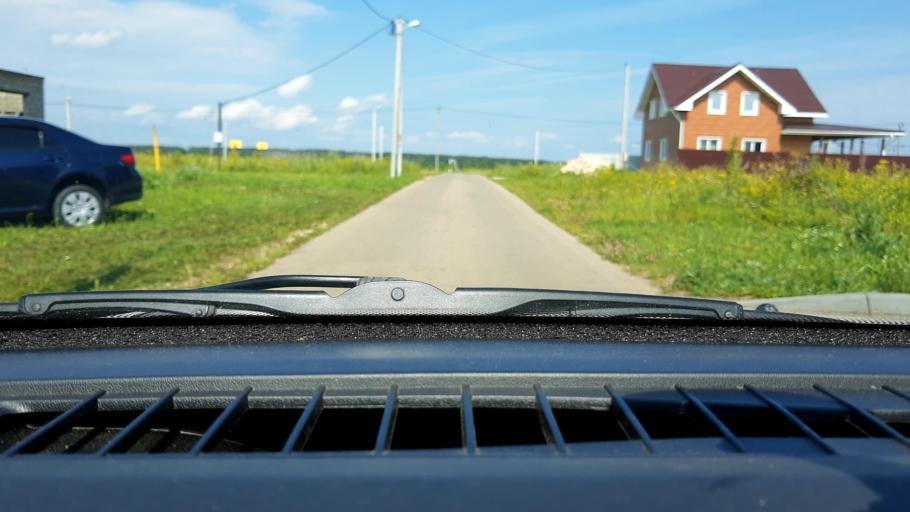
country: RU
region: Nizjnij Novgorod
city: Burevestnik
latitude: 56.1475
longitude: 43.7270
